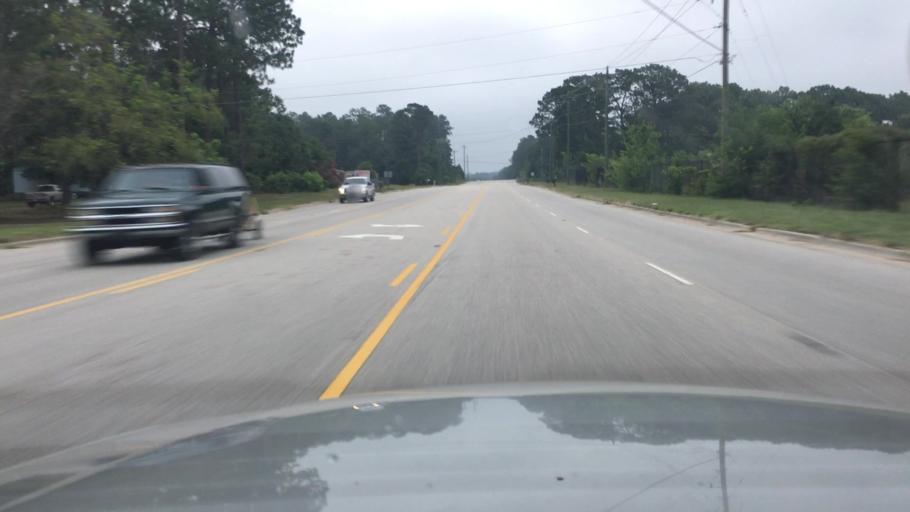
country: US
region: North Carolina
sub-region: Cumberland County
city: Fayetteville
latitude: 35.0109
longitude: -78.8832
